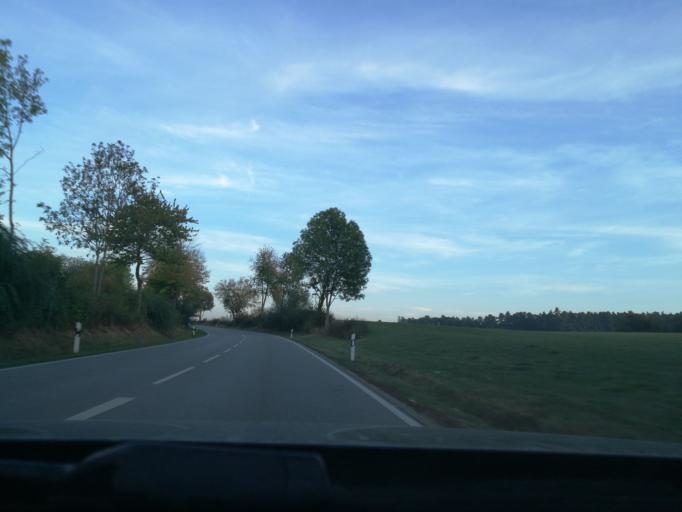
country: DE
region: Bavaria
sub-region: Regierungsbezirk Mittelfranken
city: Veitsbronn
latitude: 49.5008
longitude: 10.8933
